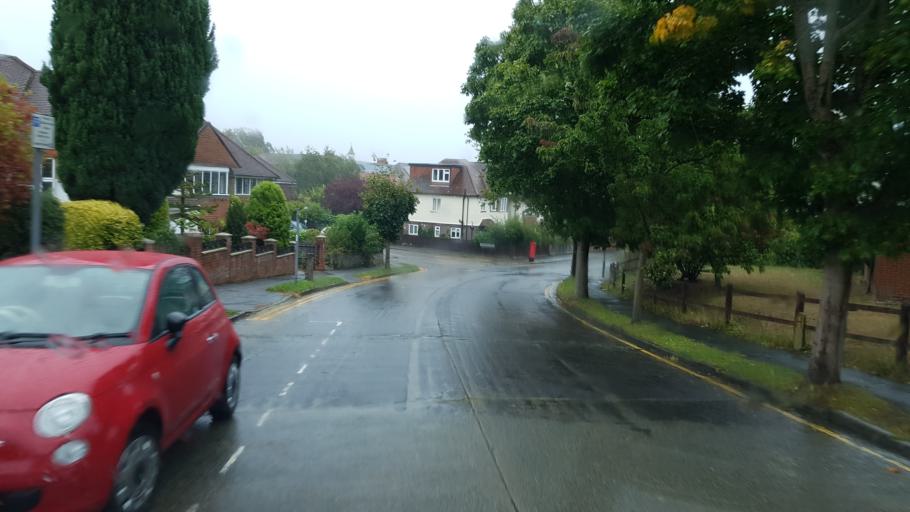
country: GB
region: England
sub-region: Surrey
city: Guildford
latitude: 51.2328
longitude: -0.5868
